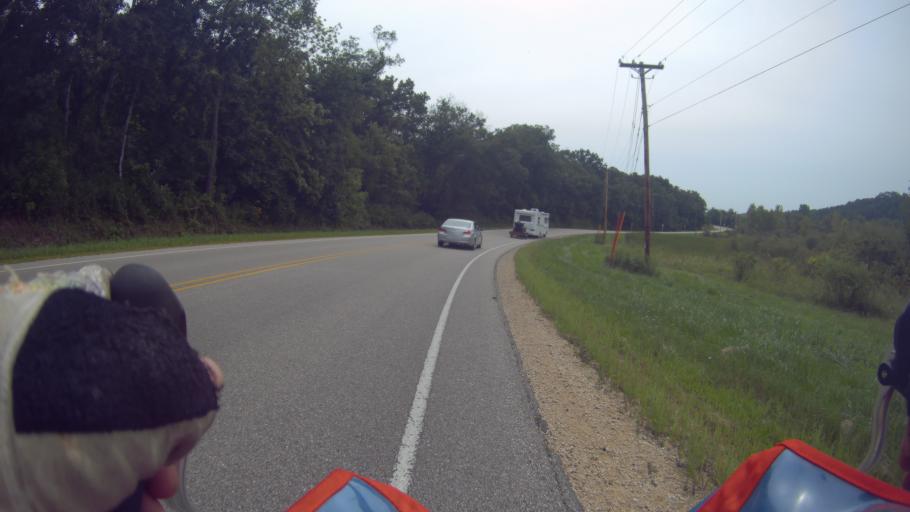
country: US
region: Wisconsin
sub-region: Dane County
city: Mount Horeb
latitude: 42.9539
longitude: -89.6611
